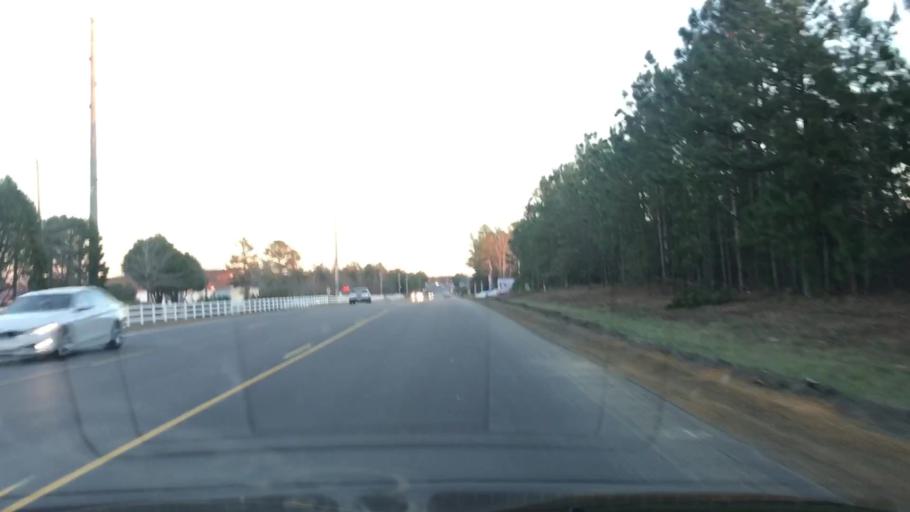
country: US
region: North Carolina
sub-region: Brunswick County
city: Shallotte
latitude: 33.9802
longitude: -78.4132
